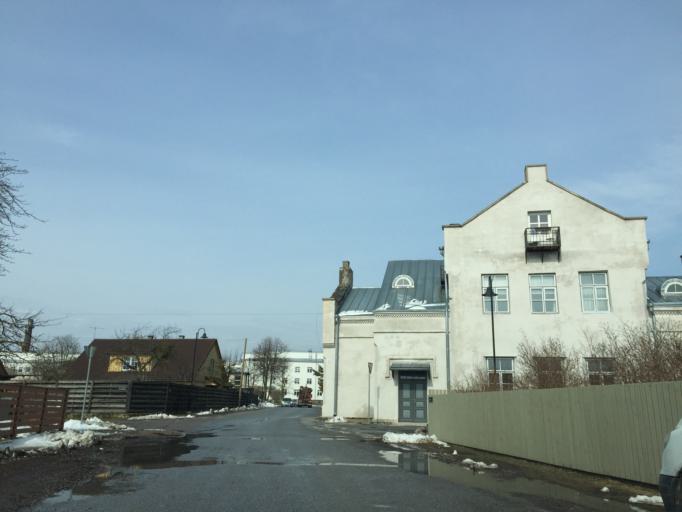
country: EE
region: Saare
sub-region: Kuressaare linn
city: Kuressaare
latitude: 58.2505
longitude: 22.4755
